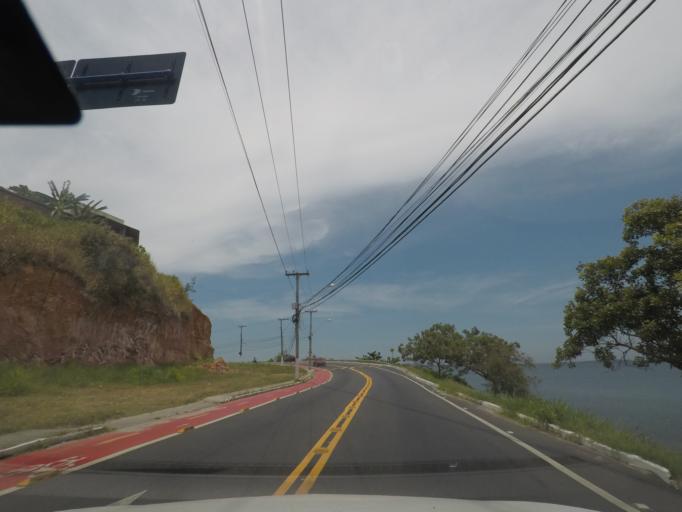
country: BR
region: Rio de Janeiro
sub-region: Marica
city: Marica
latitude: -22.9383
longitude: -42.8297
